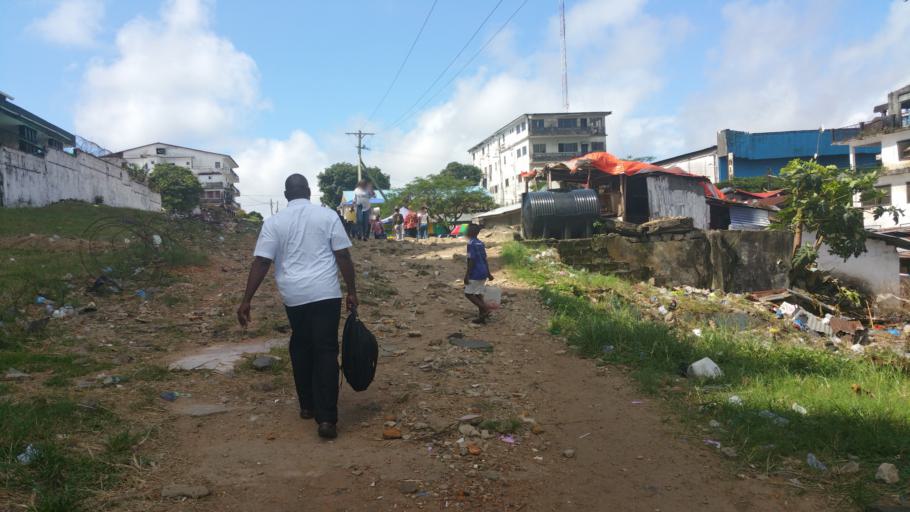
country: LR
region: Montserrado
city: Monrovia
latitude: 6.3175
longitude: -10.8090
